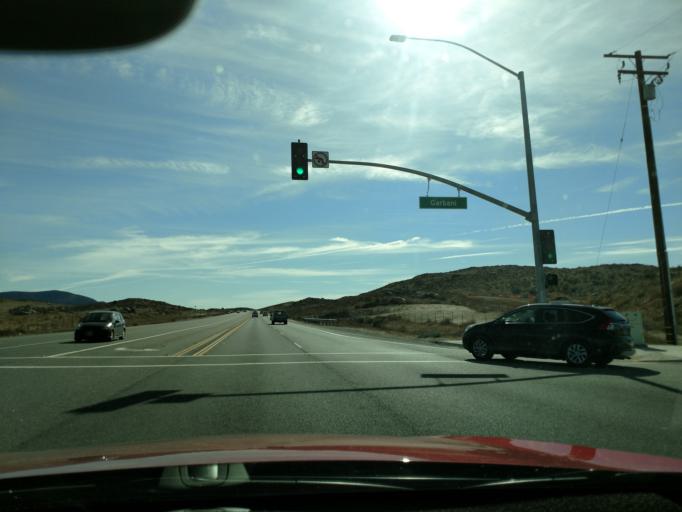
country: US
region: California
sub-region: Riverside County
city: Winchester
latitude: 33.6568
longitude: -117.0846
